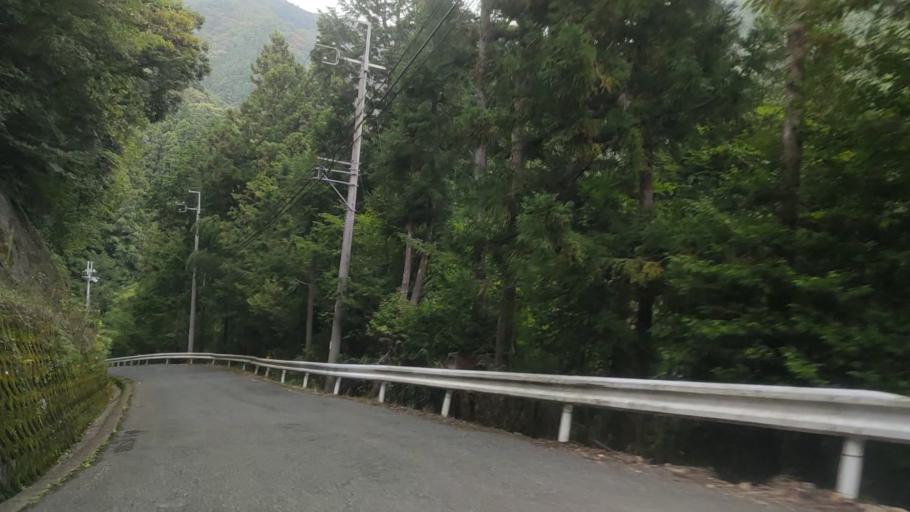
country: JP
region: Wakayama
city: Koya
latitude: 34.2265
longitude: 135.6201
